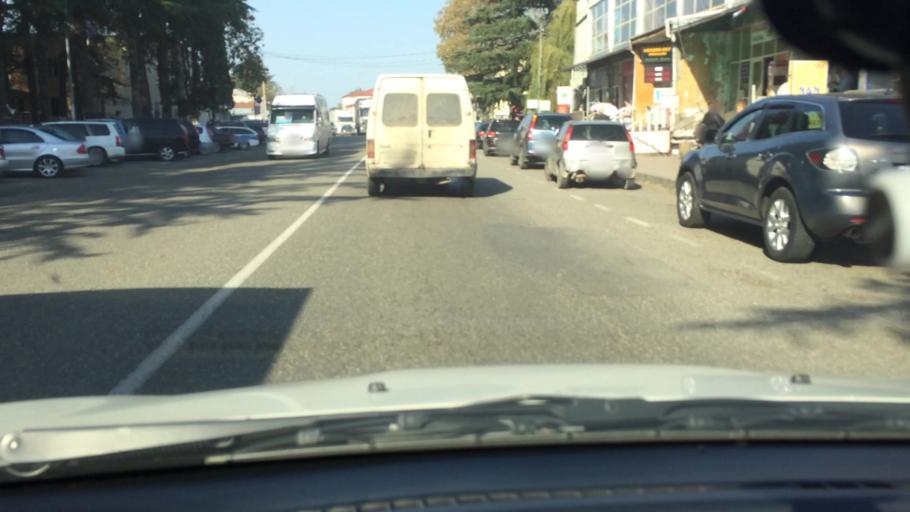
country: GE
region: Guria
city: Lanchkhuti
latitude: 42.0876
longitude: 42.0352
